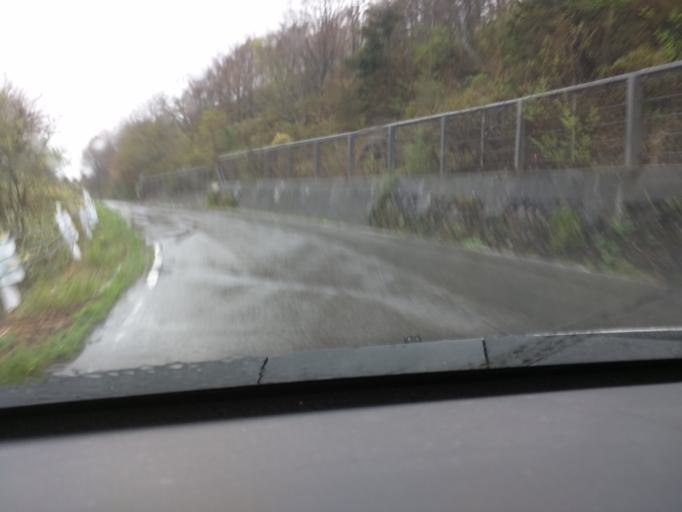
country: JP
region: Fukushima
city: Inawashiro
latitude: 37.6613
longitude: 140.2539
